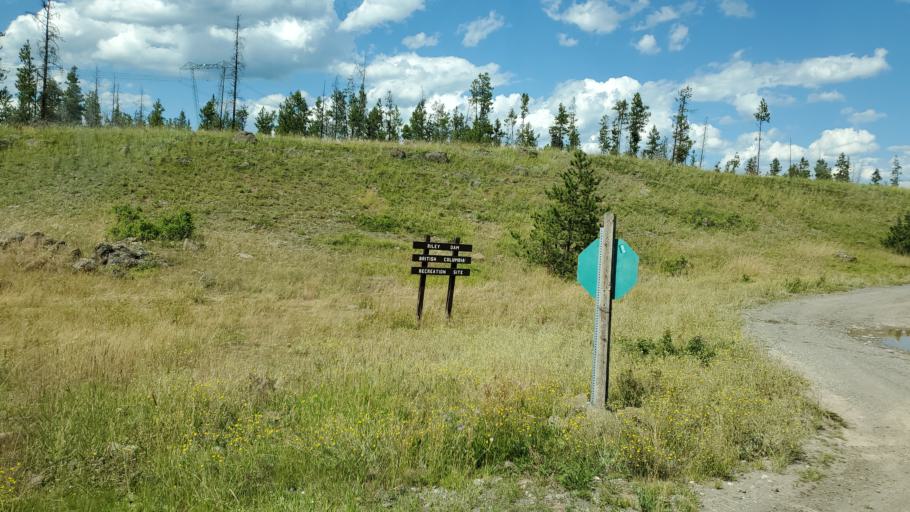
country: CA
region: British Columbia
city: Lillooet
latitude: 51.3373
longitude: -121.9610
